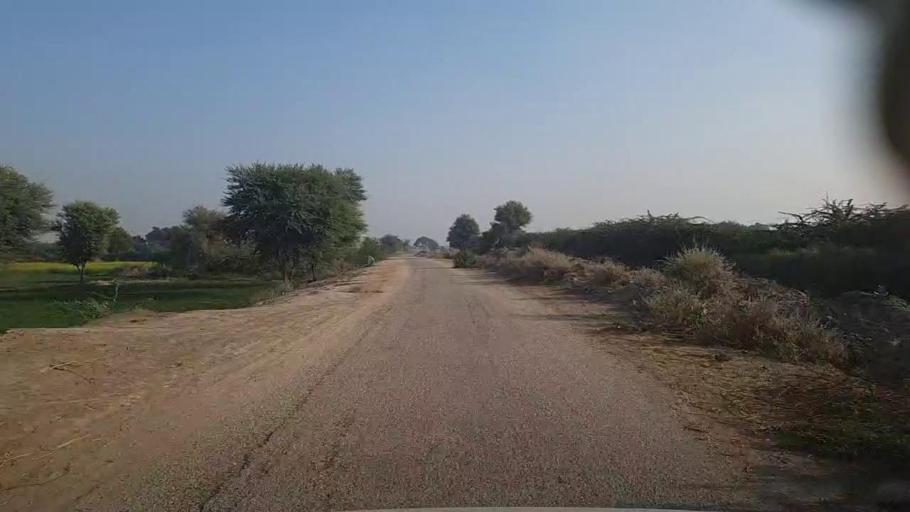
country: PK
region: Sindh
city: Karaundi
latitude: 26.7404
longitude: 68.4783
